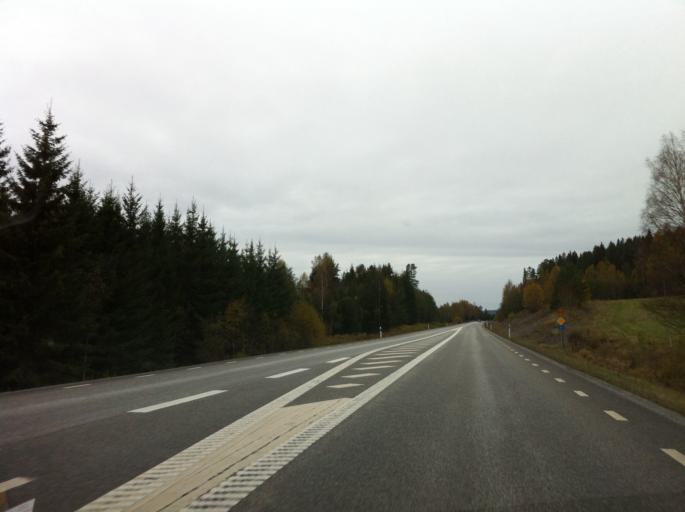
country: SE
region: OErebro
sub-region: Ljusnarsbergs Kommun
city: Kopparberg
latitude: 59.8479
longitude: 15.0684
